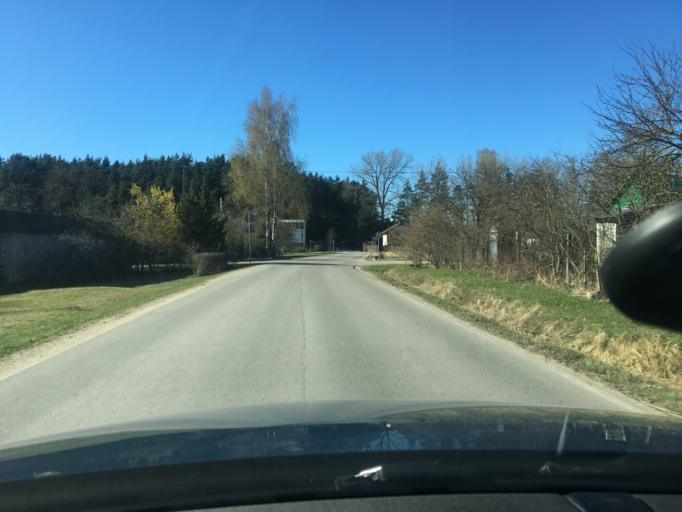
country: LV
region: Kekava
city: Kekava
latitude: 56.8541
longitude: 24.2567
